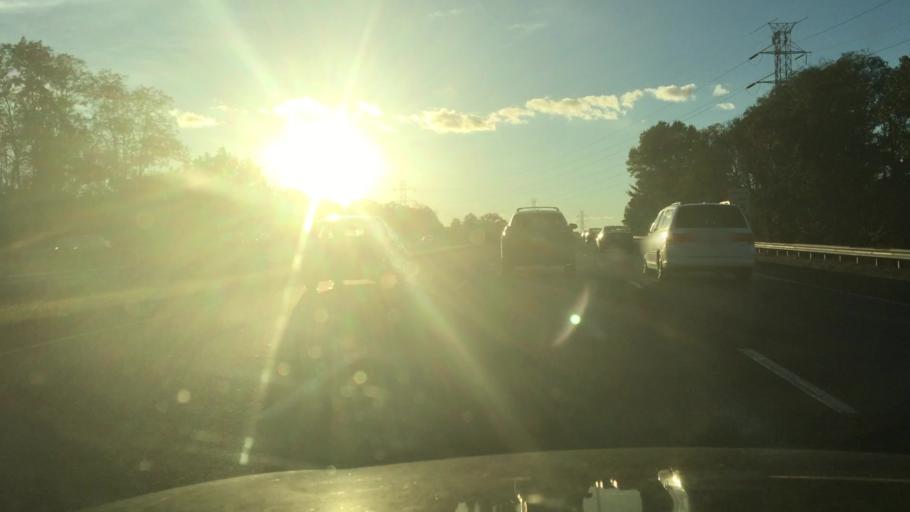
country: US
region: New Jersey
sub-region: Mercer County
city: Lawrenceville
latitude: 40.2857
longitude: -74.7211
